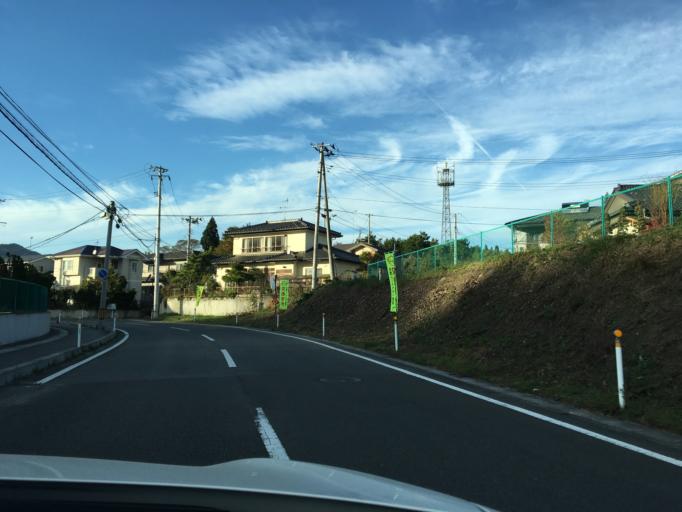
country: JP
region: Fukushima
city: Ishikawa
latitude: 37.2347
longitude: 140.5667
